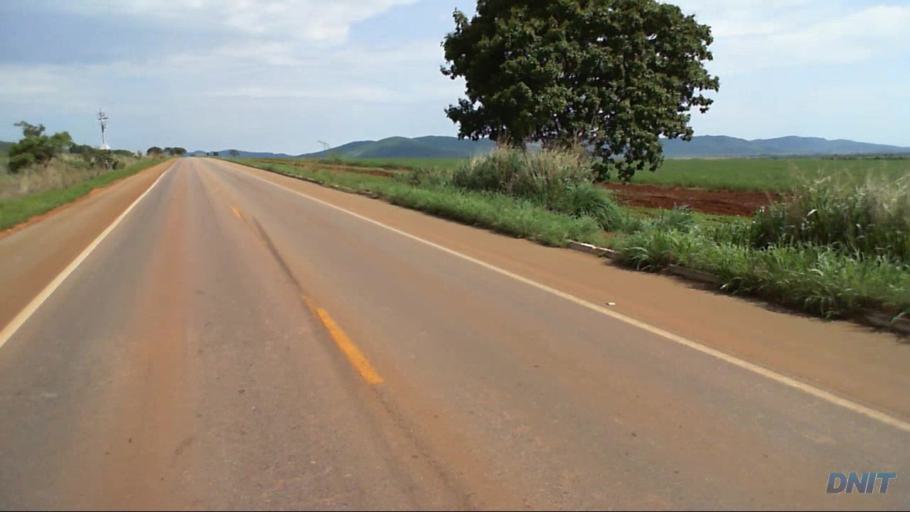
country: BR
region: Goias
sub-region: Barro Alto
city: Barro Alto
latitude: -15.0336
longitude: -48.8927
